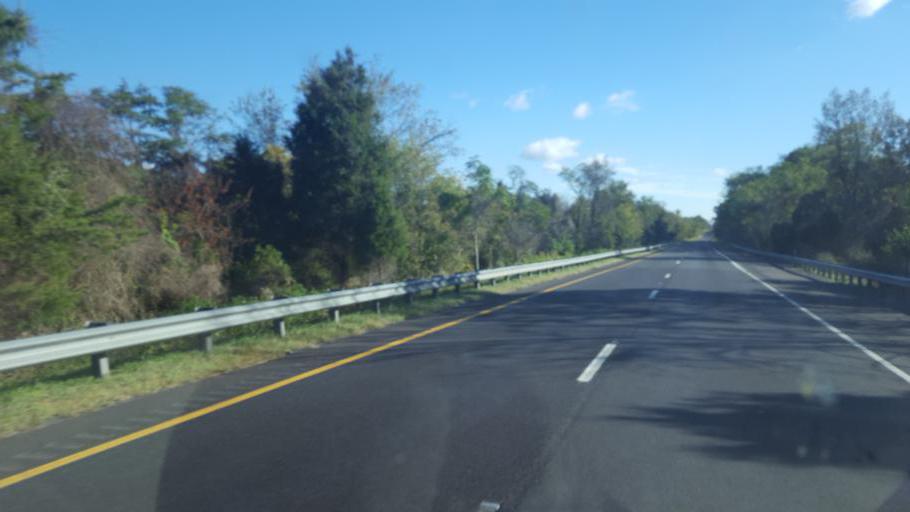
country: US
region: Maryland
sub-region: Washington County
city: Wilson-Conococheague
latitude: 39.6348
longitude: -77.9578
